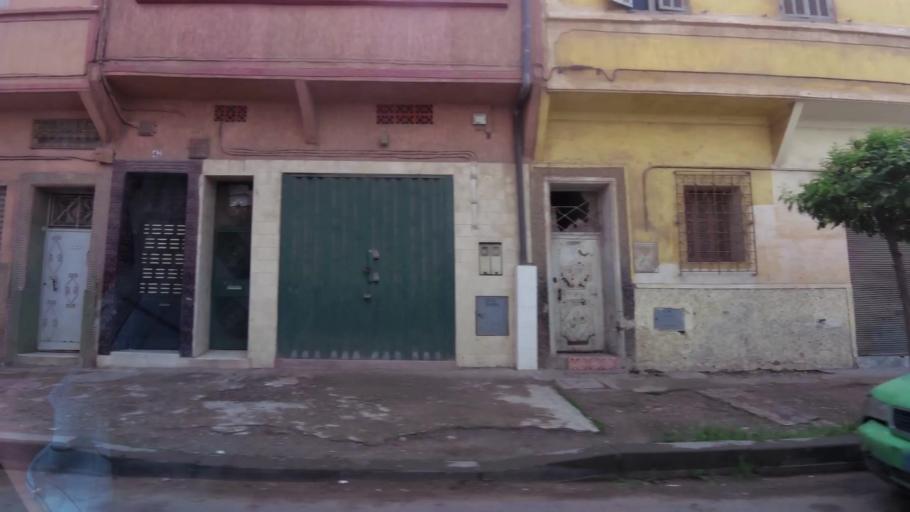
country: MA
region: Chaouia-Ouardigha
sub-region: Settat Province
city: Berrechid
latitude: 33.2694
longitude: -7.5881
